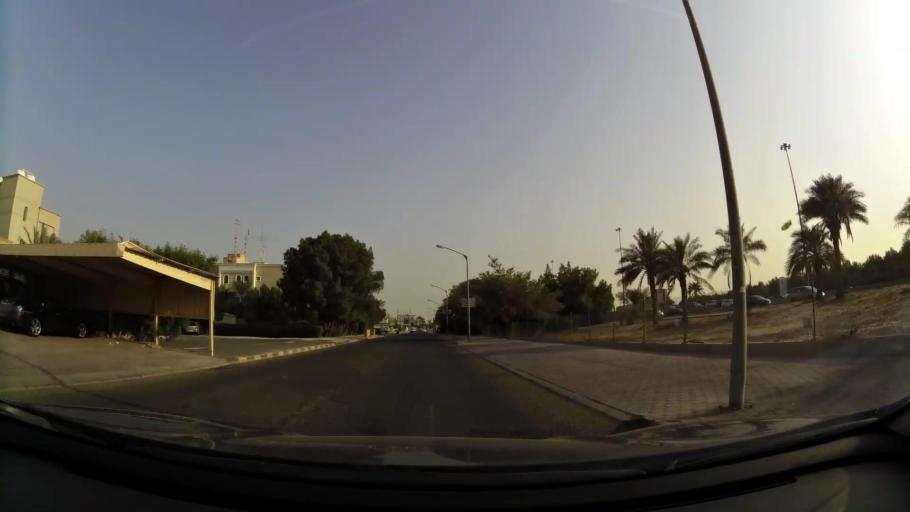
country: KW
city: Bayan
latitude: 29.3076
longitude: 48.0592
